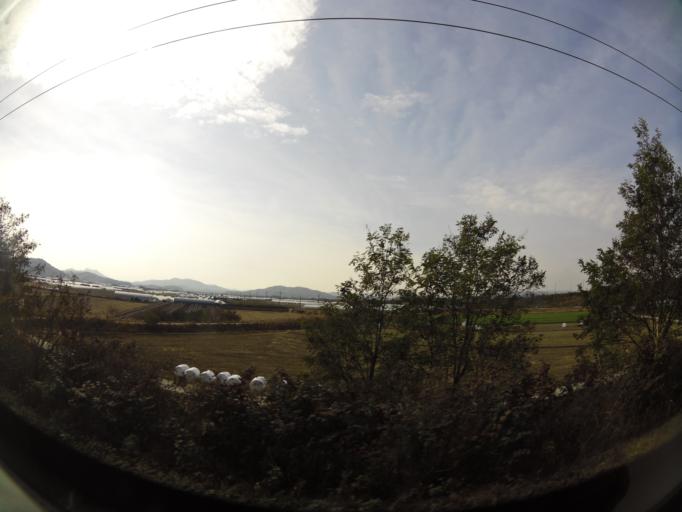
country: KR
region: Daejeon
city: Songgang-dong
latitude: 36.5683
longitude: 127.3170
